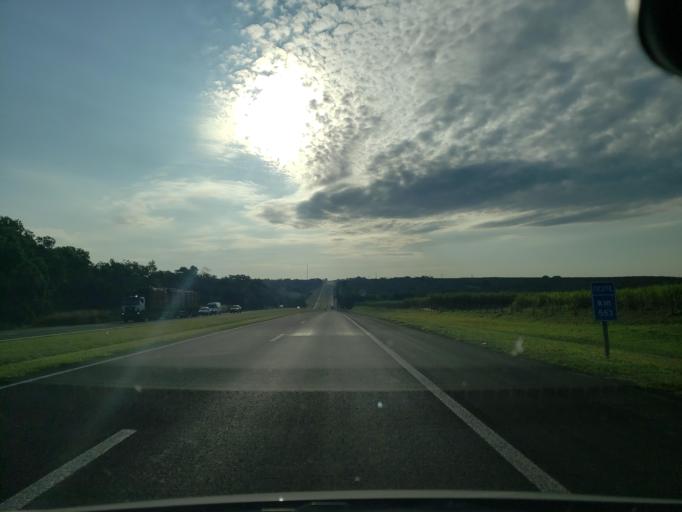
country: BR
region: Sao Paulo
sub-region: Valparaiso
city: Valparaiso
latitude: -21.1819
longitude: -50.9195
